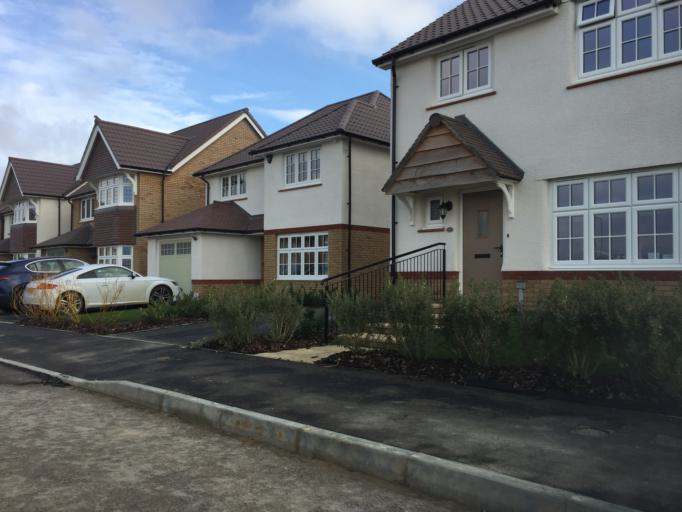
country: GB
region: England
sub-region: Gloucestershire
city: Shurdington
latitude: 51.8732
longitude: -2.0959
